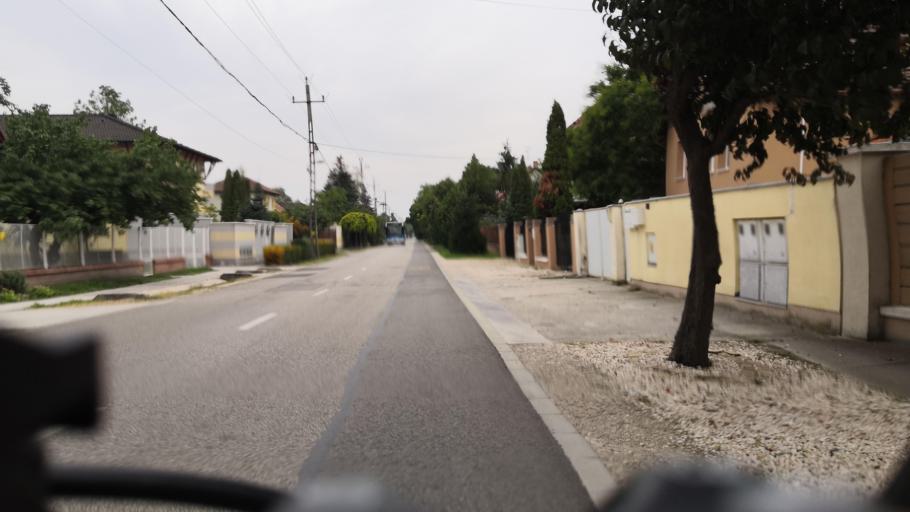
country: HU
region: Csongrad
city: Szeged
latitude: 46.2859
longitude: 20.1648
